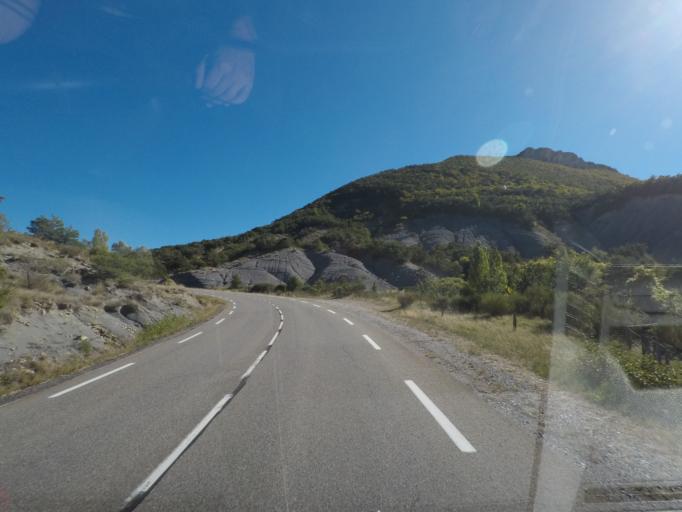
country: FR
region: Provence-Alpes-Cote d'Azur
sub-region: Departement des Hautes-Alpes
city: Serres
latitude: 44.4037
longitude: 5.5234
